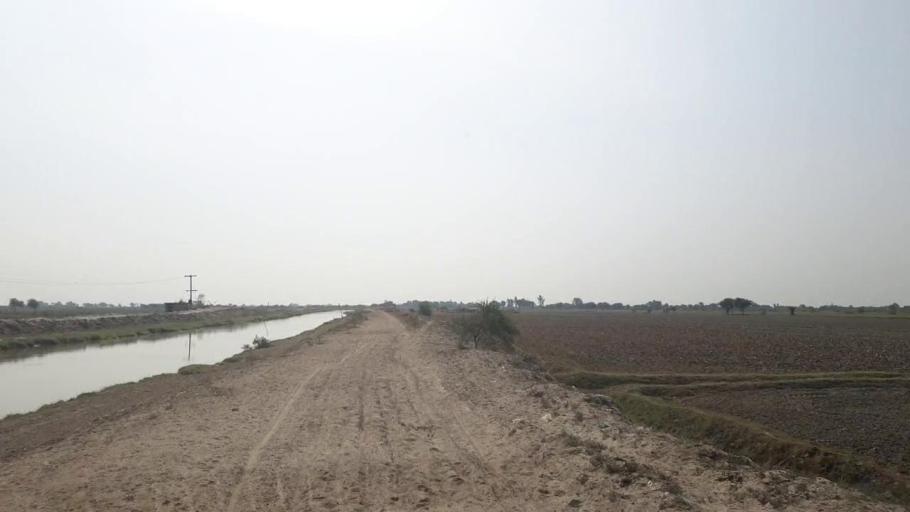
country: PK
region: Sindh
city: Badin
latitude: 24.5503
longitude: 68.8499
